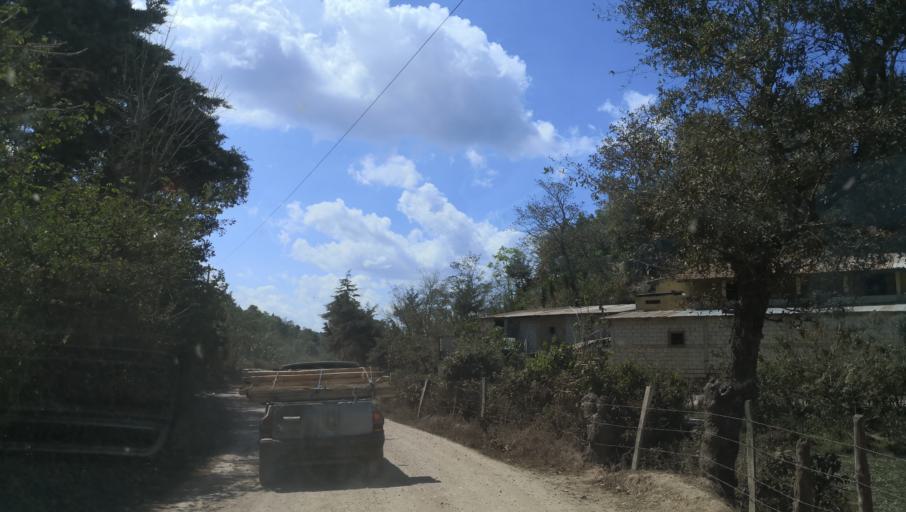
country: GT
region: Jalapa
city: San Carlos Alzatate
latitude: 14.4023
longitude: -89.9828
